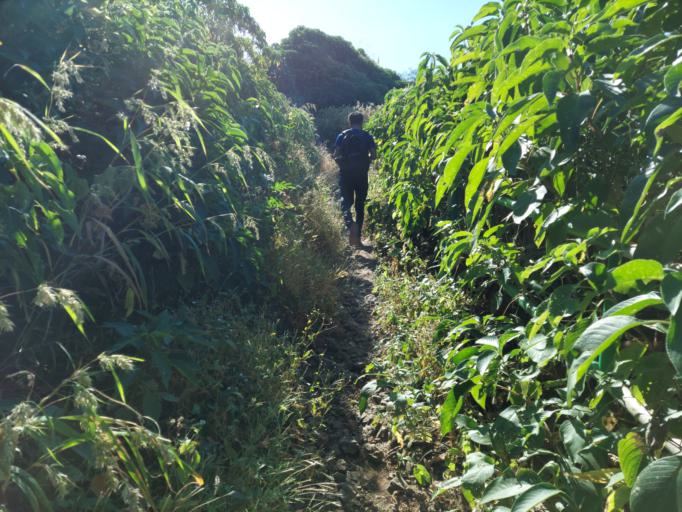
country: IN
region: Maharashtra
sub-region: Sindhudurg
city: Kudal
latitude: 16.0863
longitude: 73.8427
